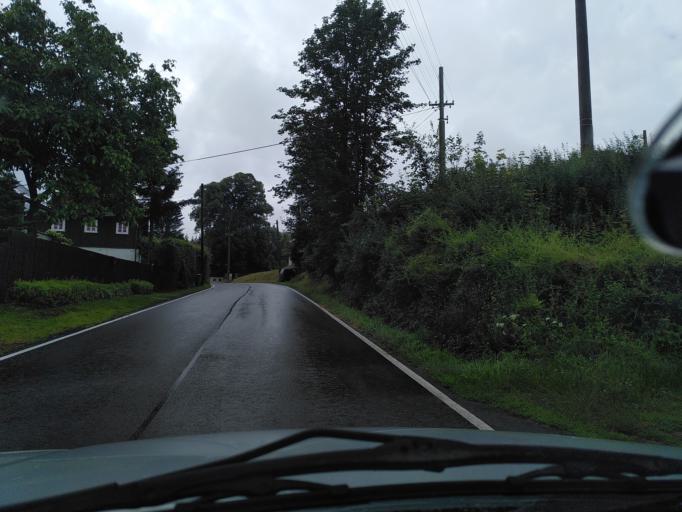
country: CZ
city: Novy Bor
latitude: 50.8108
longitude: 14.5368
